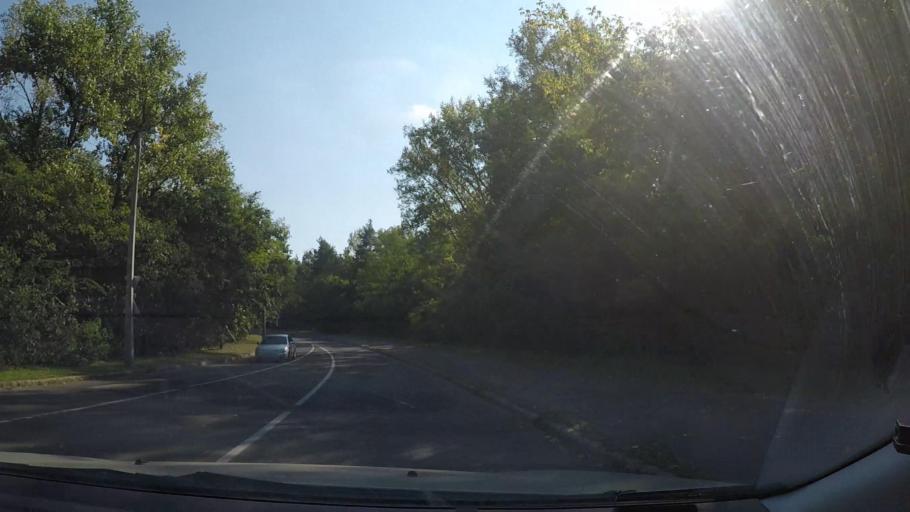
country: HU
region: Budapest
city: Budapest XV. keruelet
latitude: 47.5936
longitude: 19.1125
